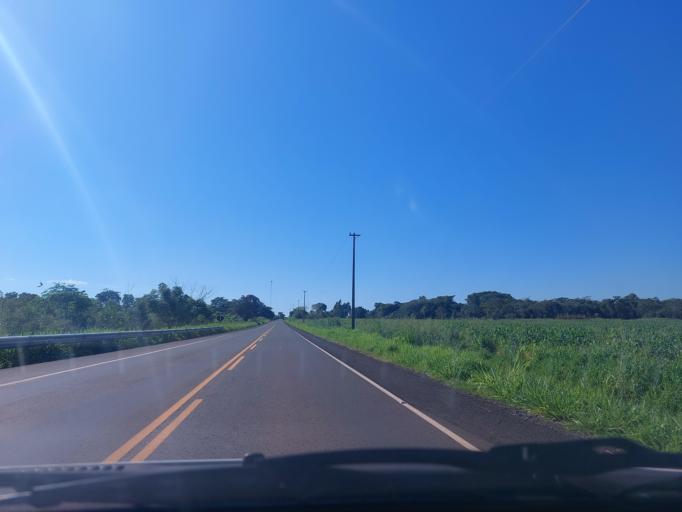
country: PY
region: San Pedro
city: Guayaybi
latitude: -24.3177
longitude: -56.1790
